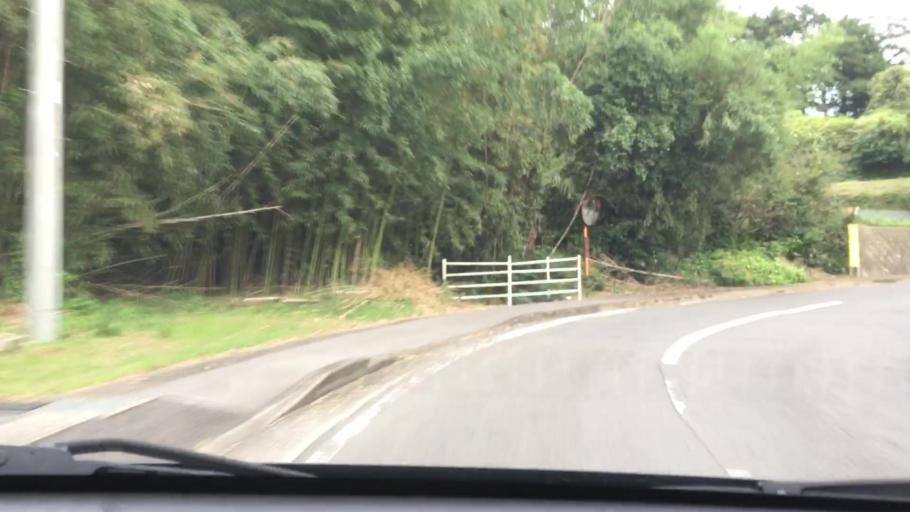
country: JP
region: Nagasaki
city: Sasebo
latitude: 33.0041
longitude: 129.7639
